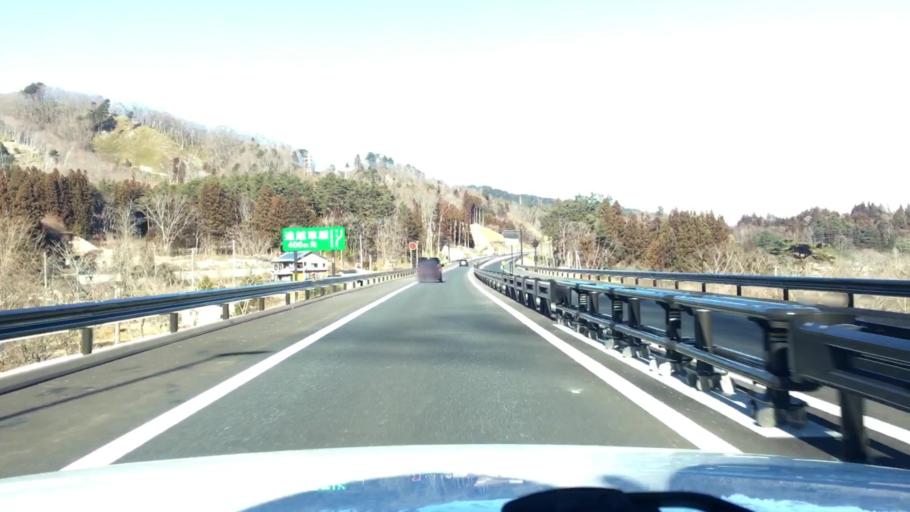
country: JP
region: Iwate
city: Miyako
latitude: 39.5711
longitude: 141.9266
